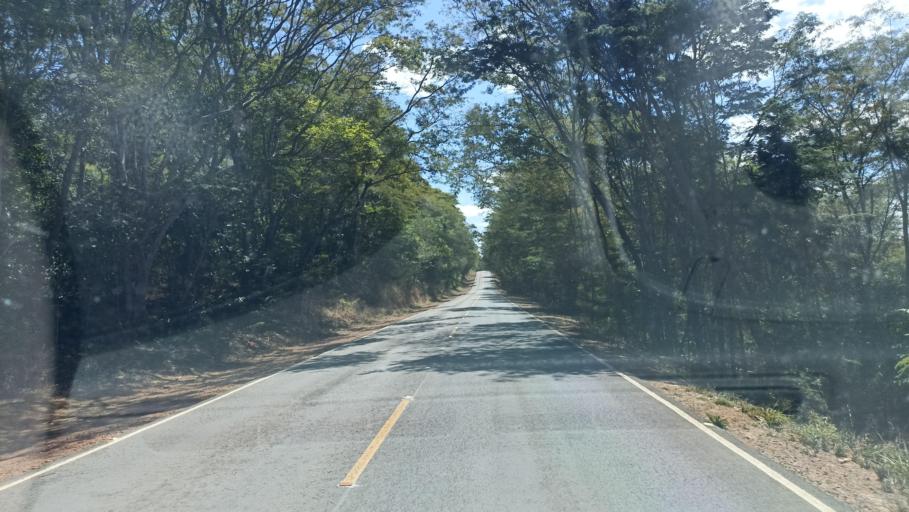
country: BR
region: Bahia
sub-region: Andarai
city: Vera Cruz
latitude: -12.7792
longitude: -41.3294
